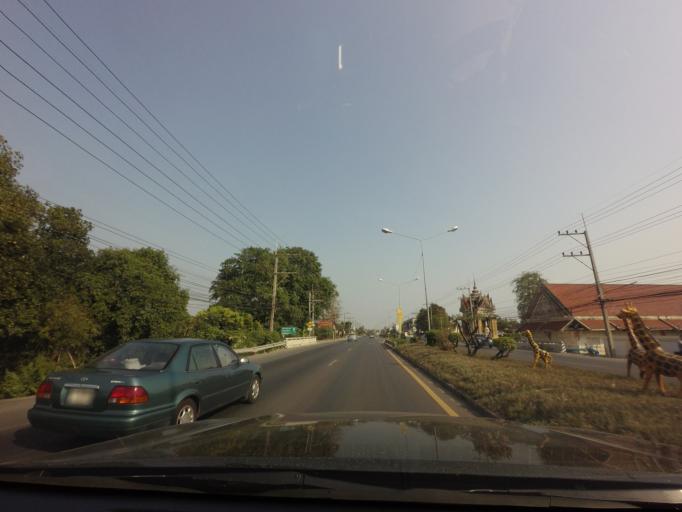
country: TH
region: Ratchaburi
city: Ban Pong
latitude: 13.8544
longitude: 99.8398
